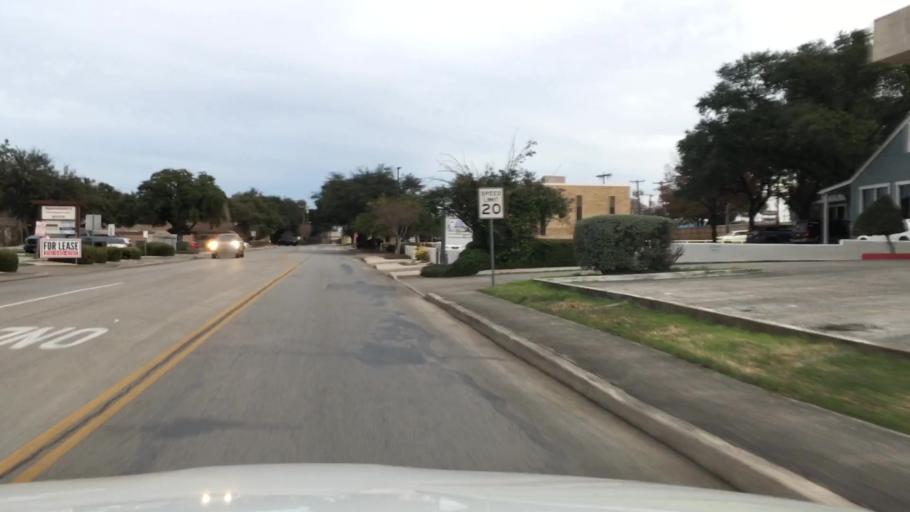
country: US
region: Texas
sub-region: Bexar County
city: Windcrest
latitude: 29.5114
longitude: -98.3898
